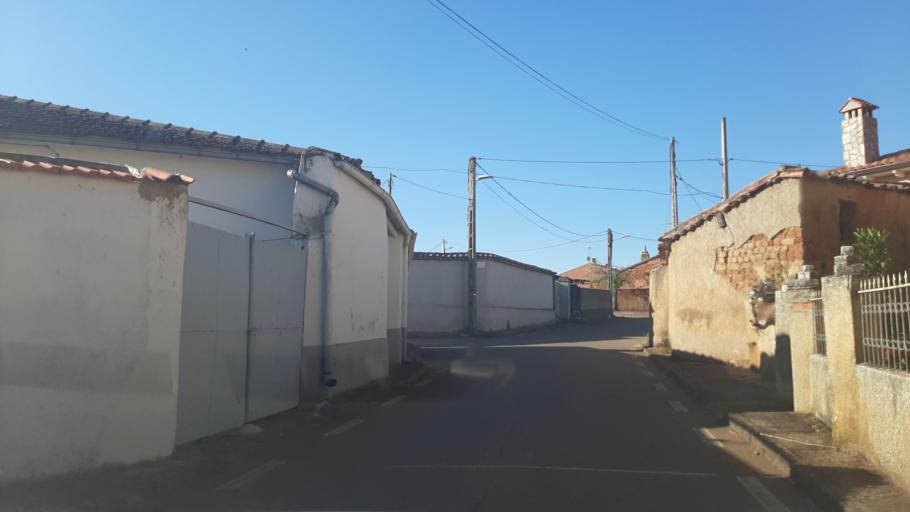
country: ES
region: Castille and Leon
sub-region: Provincia de Salamanca
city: Cabrillas
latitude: 40.7003
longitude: -6.1851
